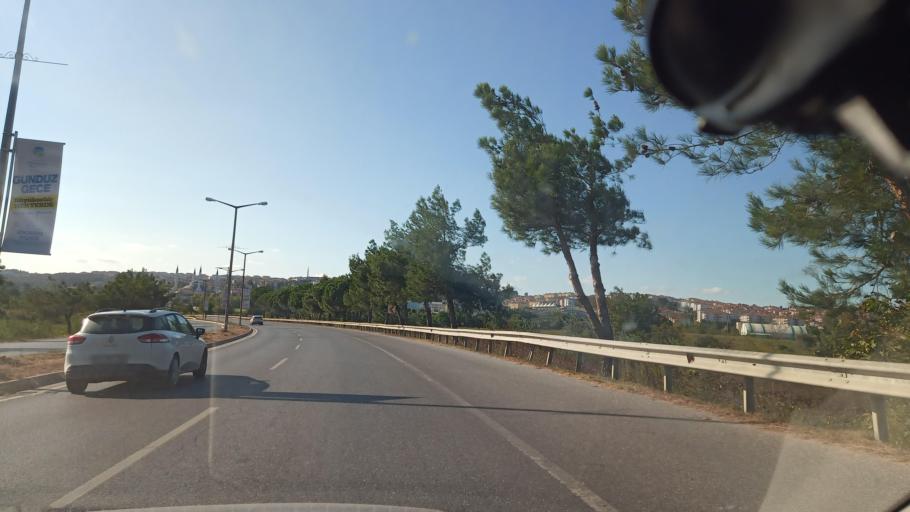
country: TR
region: Sakarya
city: Kazimpasa
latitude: 40.8483
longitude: 30.3240
